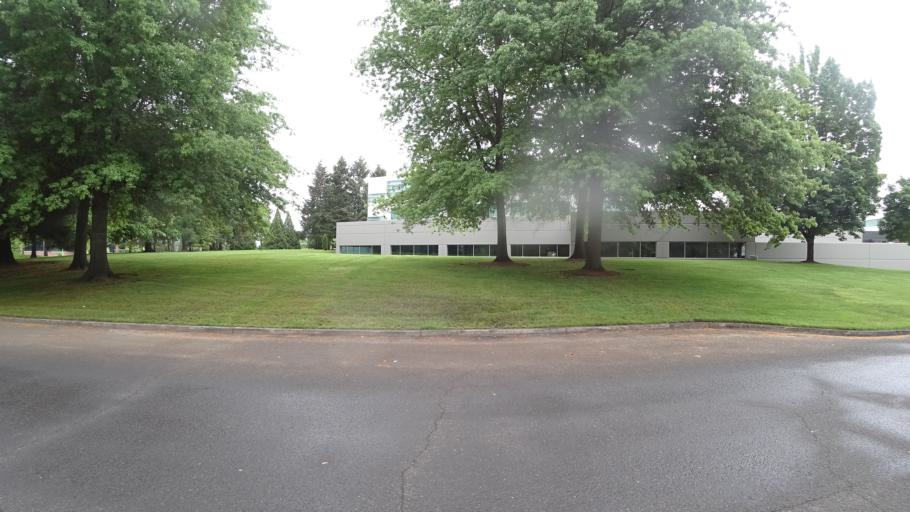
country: US
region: Oregon
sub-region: Washington County
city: Rockcreek
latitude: 45.5324
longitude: -122.8820
